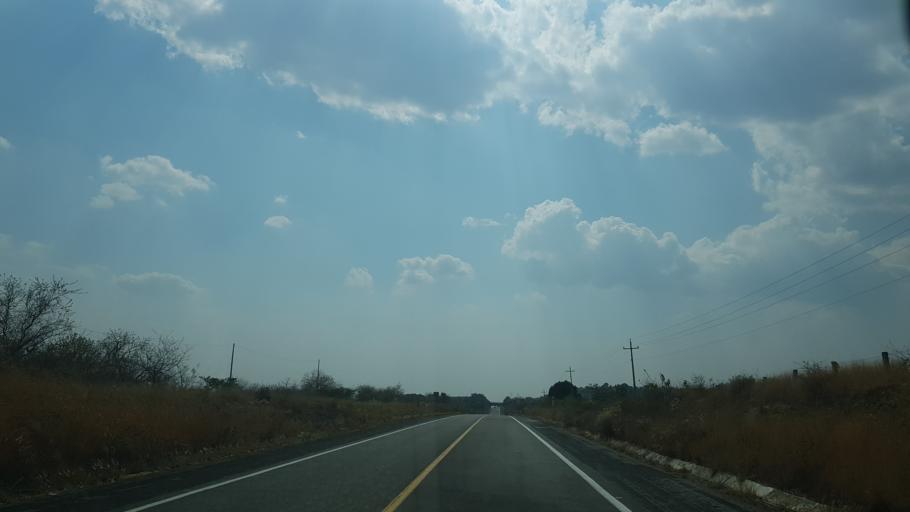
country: MX
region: Puebla
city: San Juan Amecac
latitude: 18.8169
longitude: -98.6569
